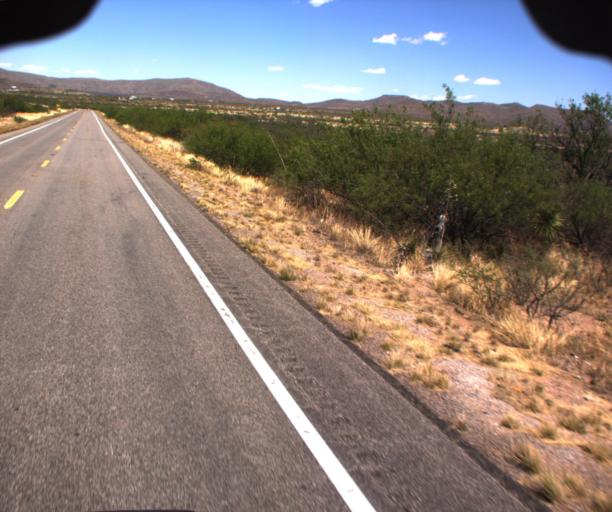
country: US
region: Arizona
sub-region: Cochise County
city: Bisbee
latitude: 31.5327
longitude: -110.0119
